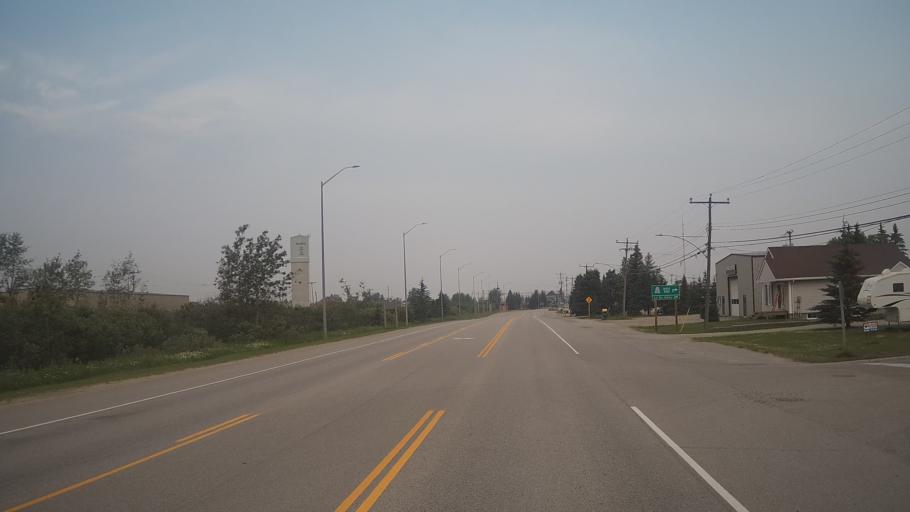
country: CA
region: Ontario
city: Hearst
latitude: 49.6875
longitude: -83.6445
